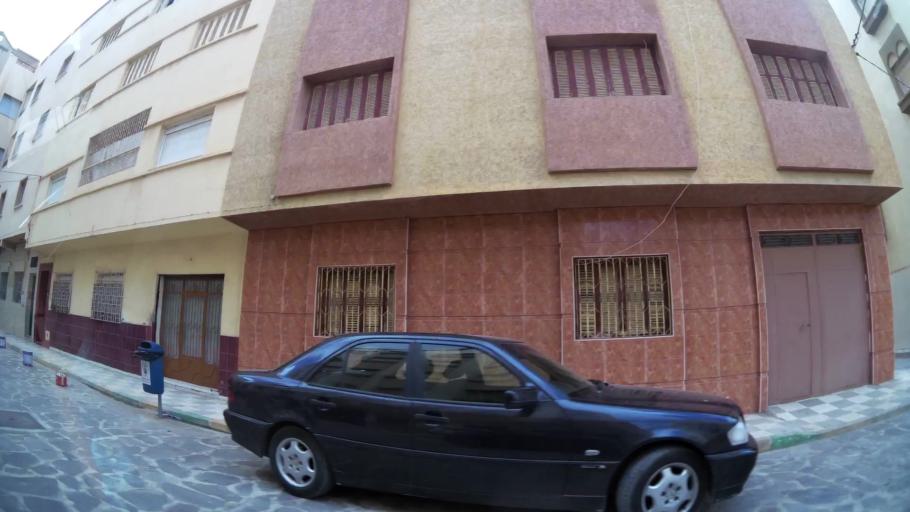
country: MA
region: Oriental
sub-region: Nador
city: Nador
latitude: 35.1727
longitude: -2.9313
